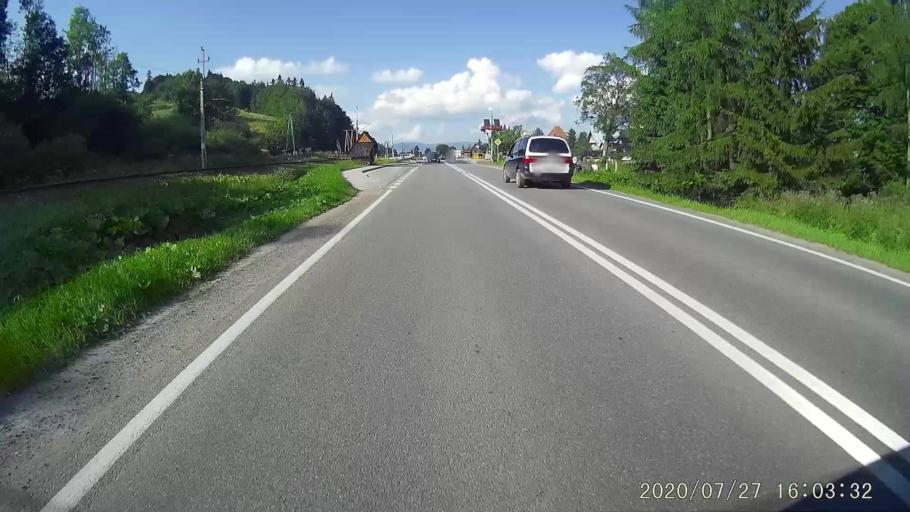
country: PL
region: Lesser Poland Voivodeship
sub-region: Powiat tatrzanski
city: Bialy Dunajec
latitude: 49.3694
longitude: 20.0034
